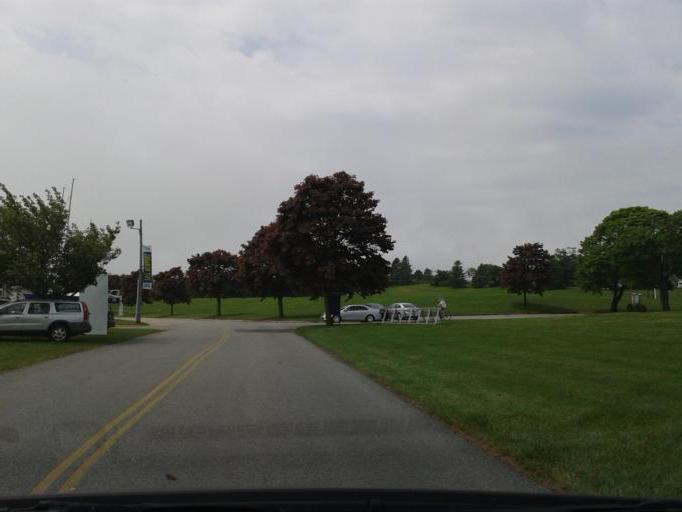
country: US
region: Rhode Island
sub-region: Newport County
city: Newport
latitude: 41.4749
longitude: -71.3371
